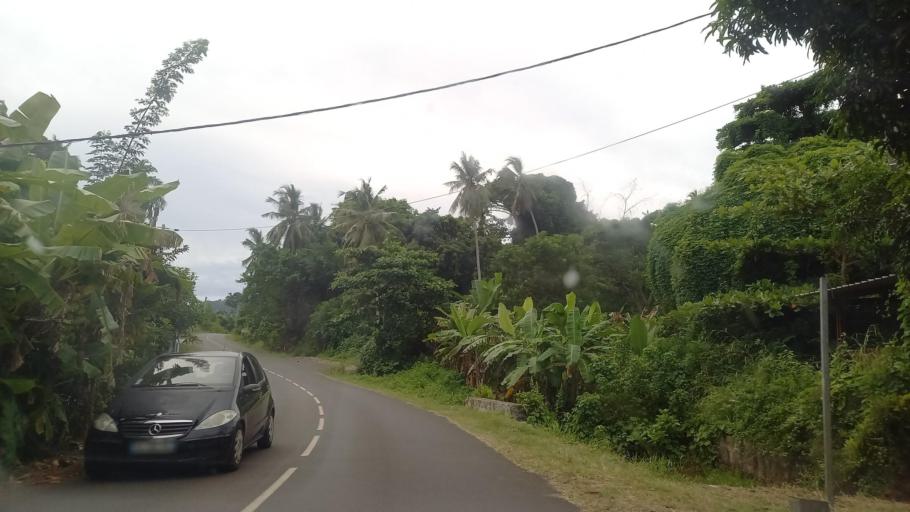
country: YT
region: Kani-Keli
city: Kani Keli
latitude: -12.9434
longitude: 45.1026
